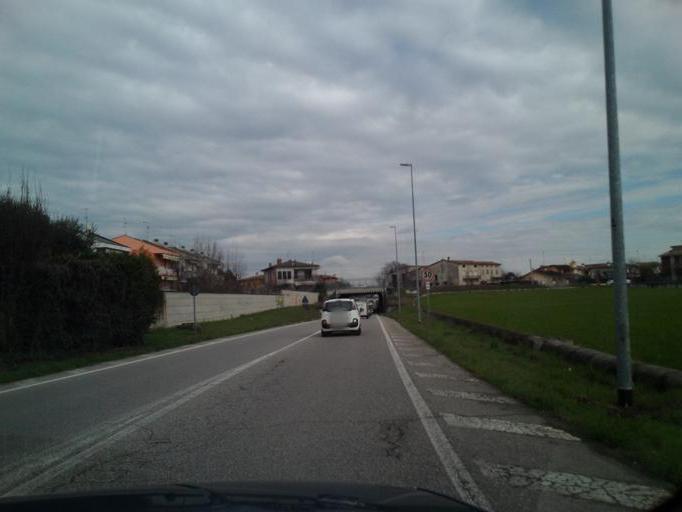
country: IT
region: Veneto
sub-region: Provincia di Verona
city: Villafranca di Verona
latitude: 45.3600
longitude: 10.8388
